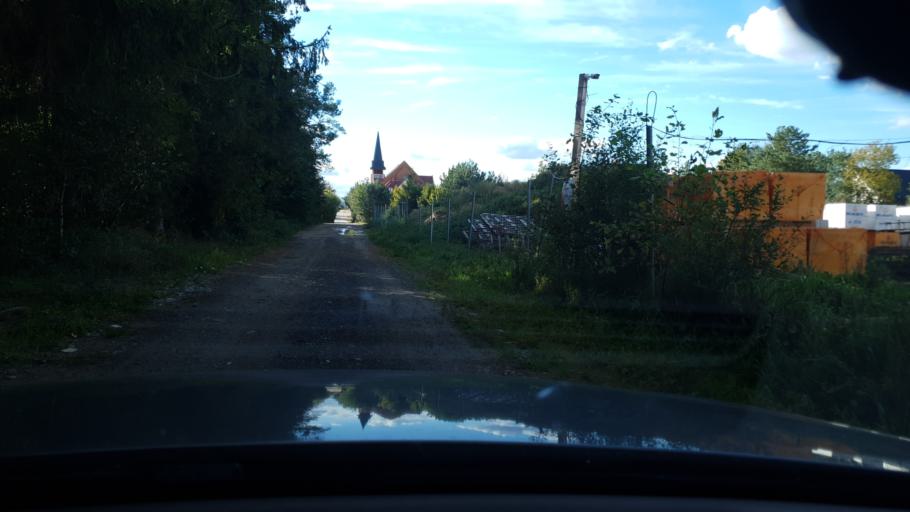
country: PL
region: Pomeranian Voivodeship
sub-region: Powiat kartuski
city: Chwaszczyno
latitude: 54.4851
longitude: 18.4239
